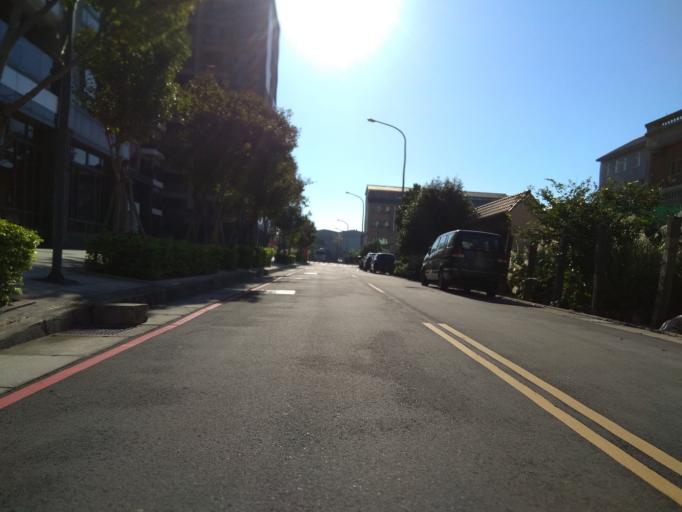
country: TW
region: Taiwan
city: Taoyuan City
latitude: 25.0203
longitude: 121.2193
